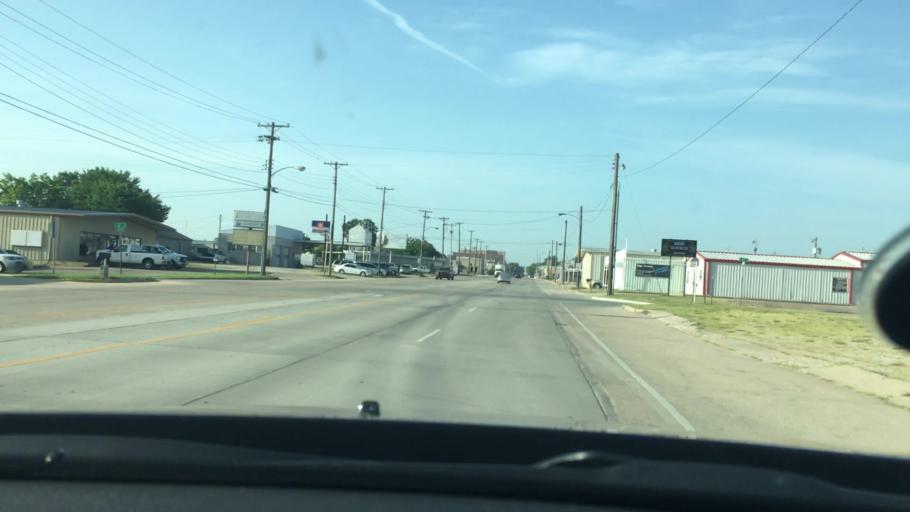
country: US
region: Oklahoma
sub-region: Pontotoc County
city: Ada
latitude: 34.7802
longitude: -96.6787
